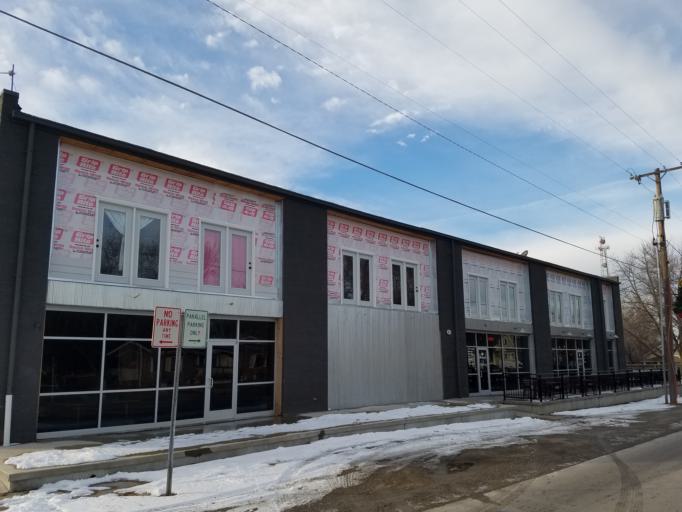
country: US
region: Missouri
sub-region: Saline County
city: Sweet Springs
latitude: 38.9639
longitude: -93.4158
